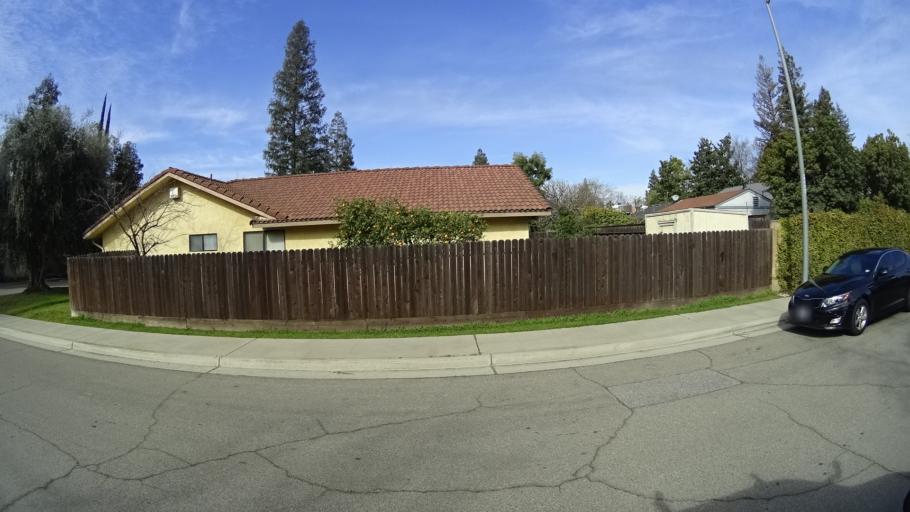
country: US
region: California
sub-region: Fresno County
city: West Park
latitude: 36.8331
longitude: -119.8696
